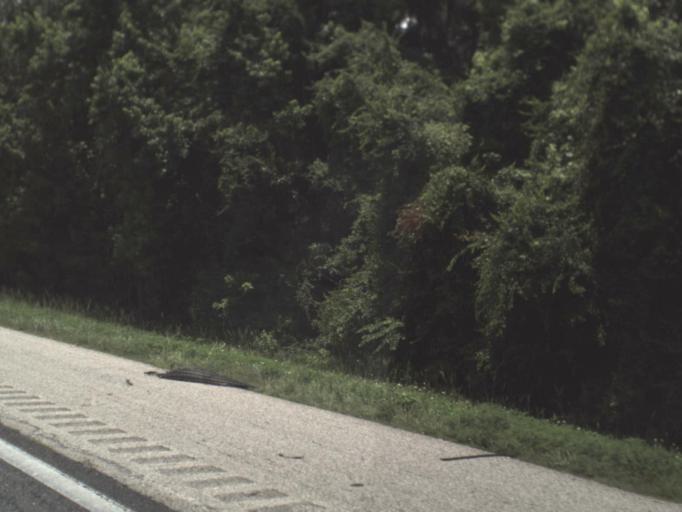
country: US
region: Florida
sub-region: Alachua County
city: Gainesville
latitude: 29.6369
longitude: -82.4001
